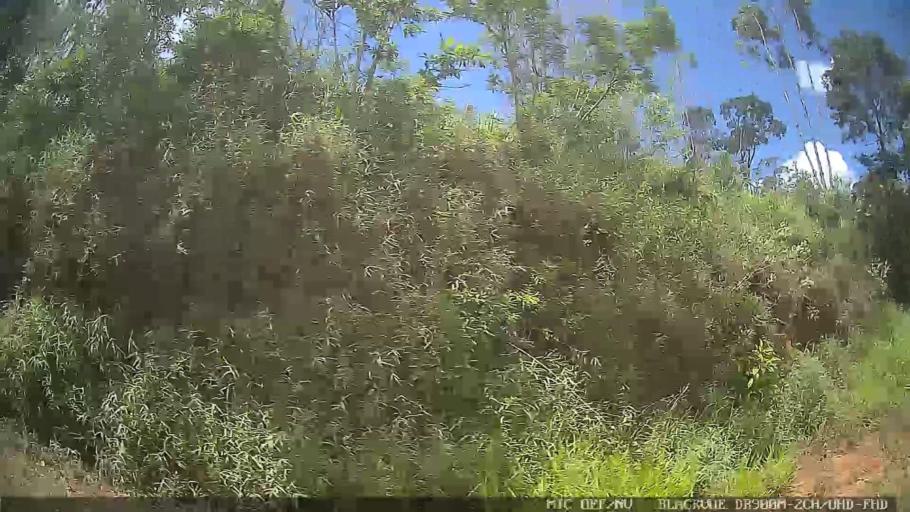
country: BR
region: Minas Gerais
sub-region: Extrema
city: Extrema
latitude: -22.7568
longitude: -46.4355
